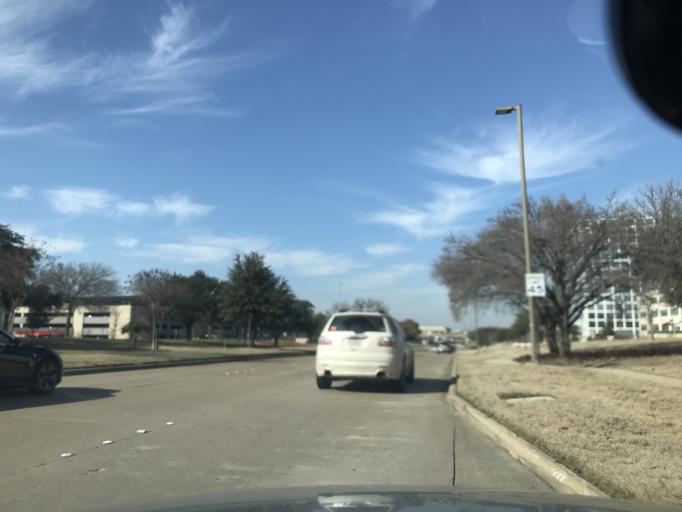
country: US
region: Texas
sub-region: Denton County
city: The Colony
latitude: 33.0823
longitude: -96.8374
